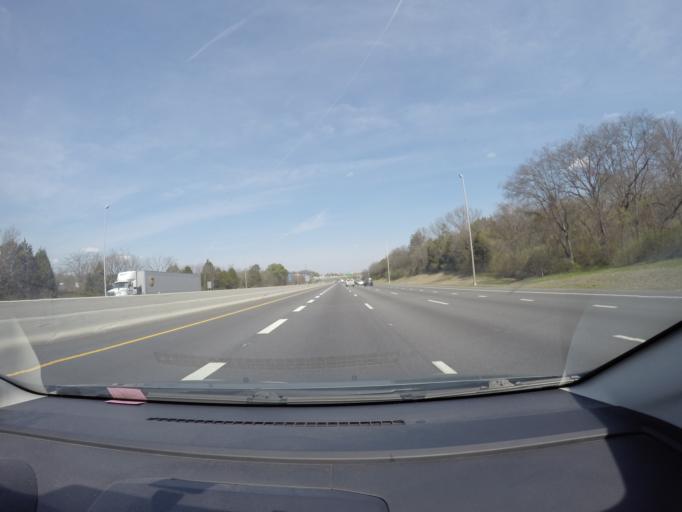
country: US
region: Tennessee
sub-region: Davidson County
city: Oak Hill
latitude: 36.0803
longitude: -86.6963
